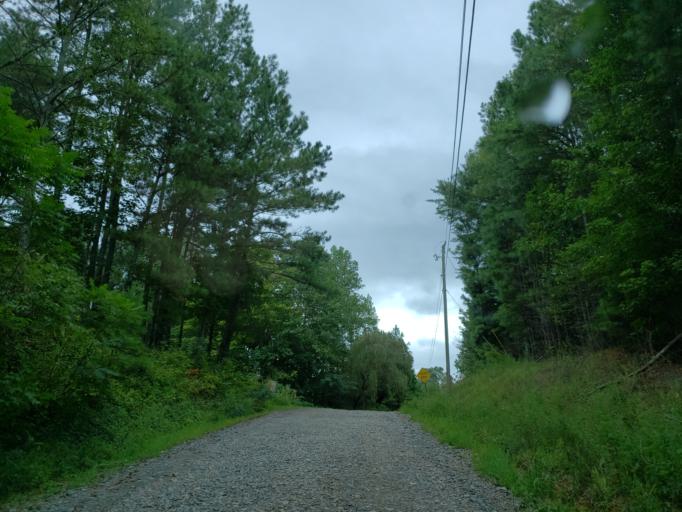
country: US
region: Georgia
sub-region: Gilmer County
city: Ellijay
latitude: 34.5681
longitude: -84.5235
